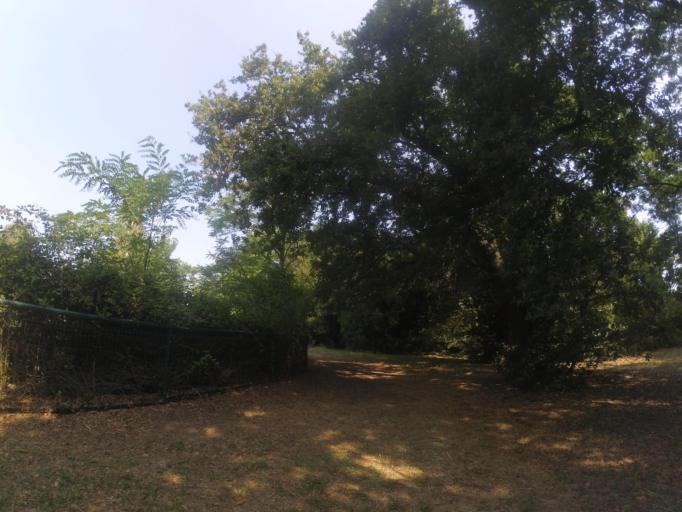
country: FR
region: Languedoc-Roussillon
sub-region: Departement des Pyrenees-Orientales
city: Toulouges
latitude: 42.6656
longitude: 2.8388
